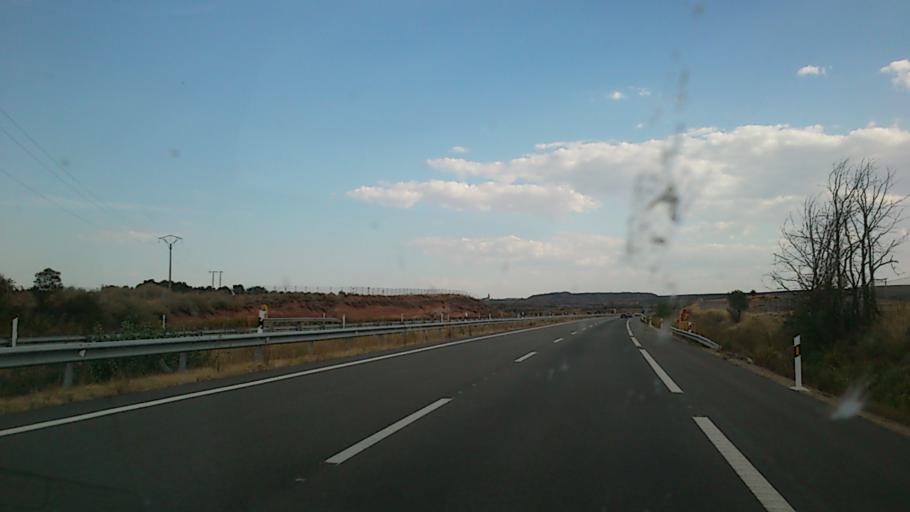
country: ES
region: Navarre
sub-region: Provincia de Navarra
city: Azagra
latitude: 42.2732
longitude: -1.9330
